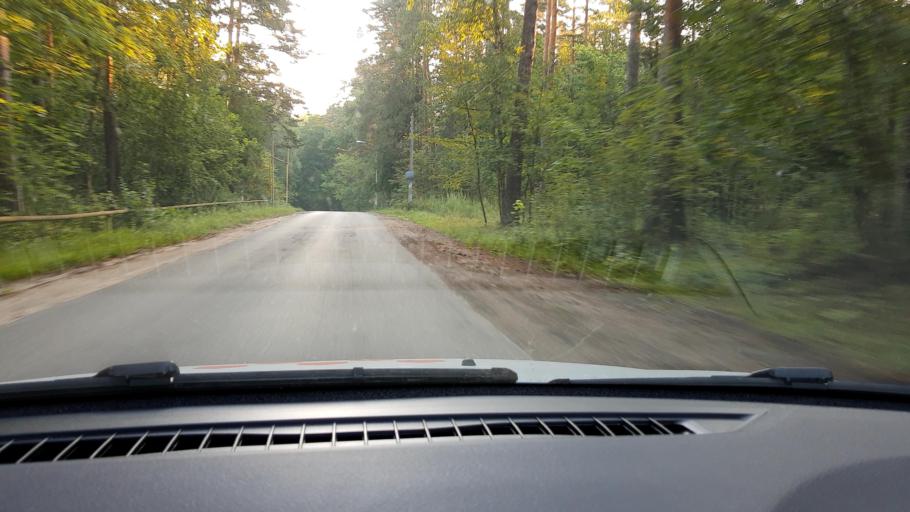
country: RU
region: Nizjnij Novgorod
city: Afonino
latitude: 56.1789
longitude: 44.0787
